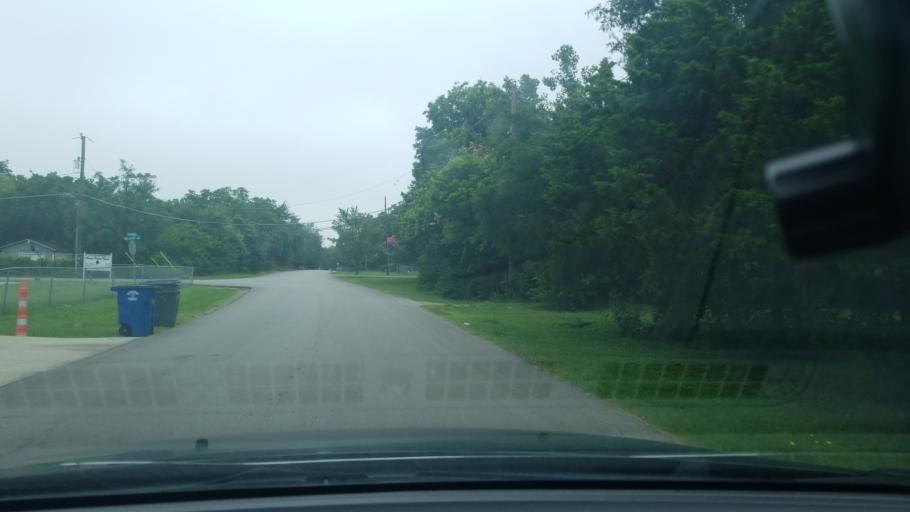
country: US
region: Texas
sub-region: Dallas County
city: Balch Springs
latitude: 32.7571
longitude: -96.6772
